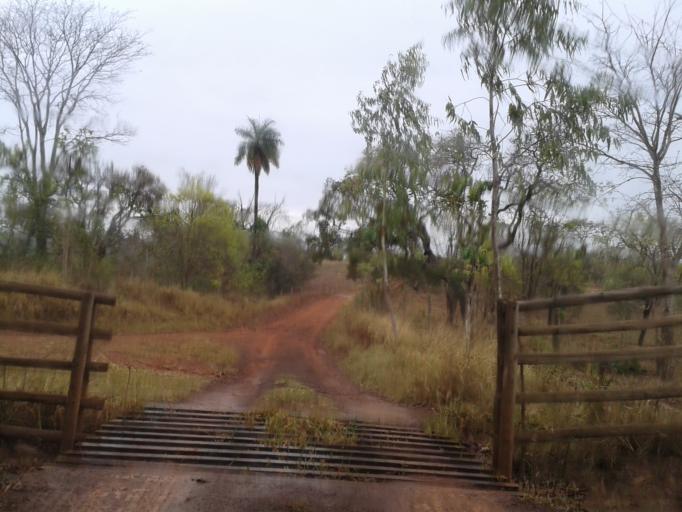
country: BR
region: Minas Gerais
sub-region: Campina Verde
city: Campina Verde
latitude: -19.3187
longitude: -49.5112
